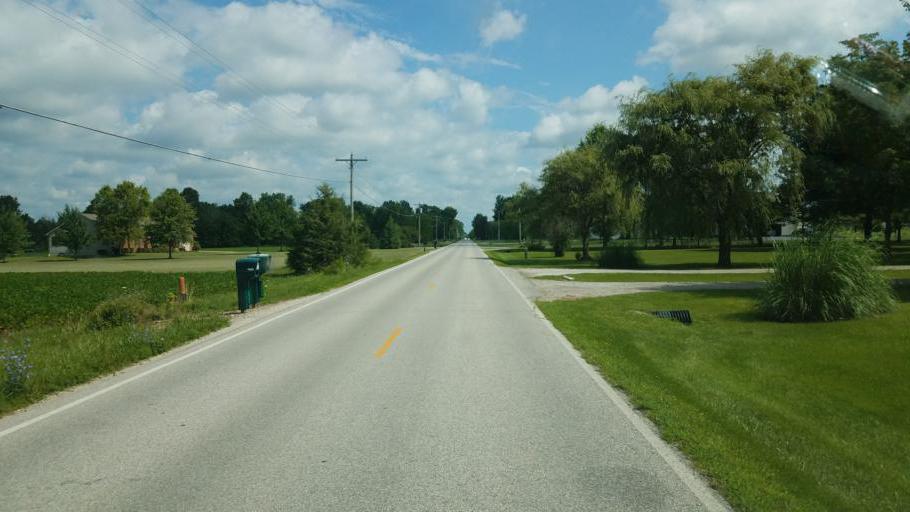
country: US
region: Ohio
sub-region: Delaware County
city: Sunbury
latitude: 40.2956
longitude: -82.9347
